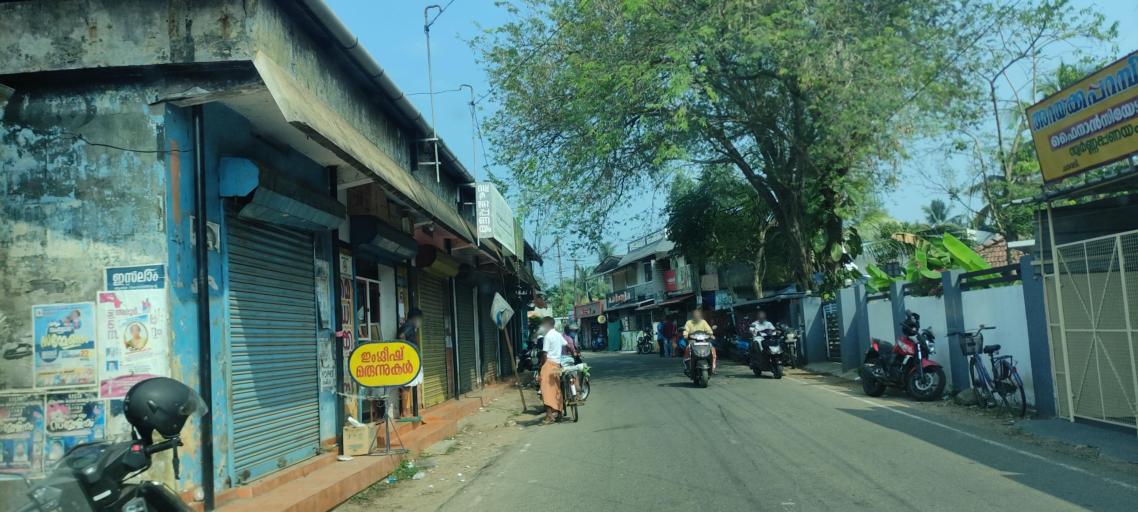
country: IN
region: Kerala
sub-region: Alappuzha
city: Kutiatodu
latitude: 9.7742
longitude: 76.3061
